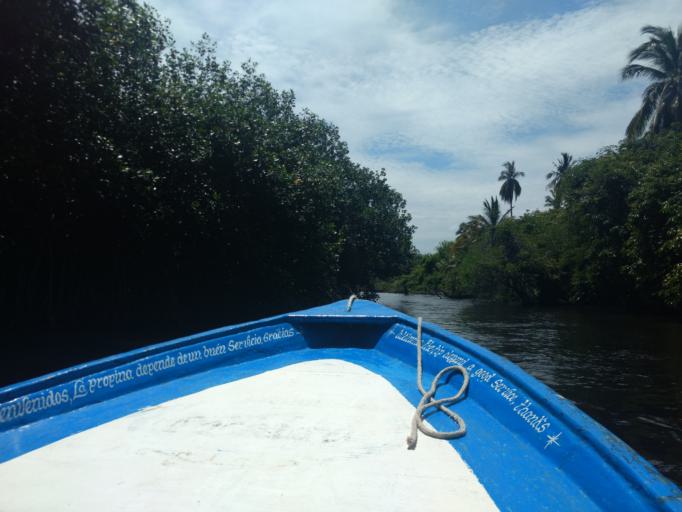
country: MX
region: Nayarit
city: San Blas
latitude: 21.5353
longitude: -105.2381
